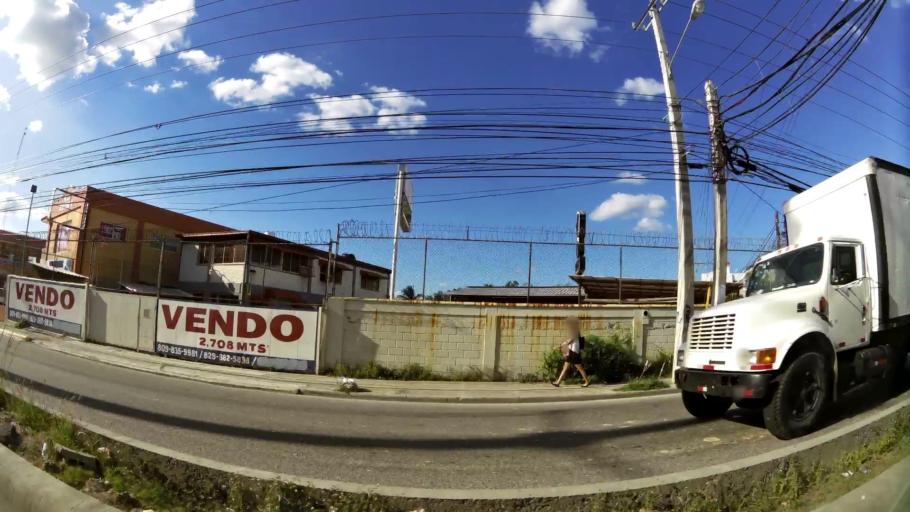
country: DO
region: Nacional
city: Santo Domingo
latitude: 18.5066
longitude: -69.9778
